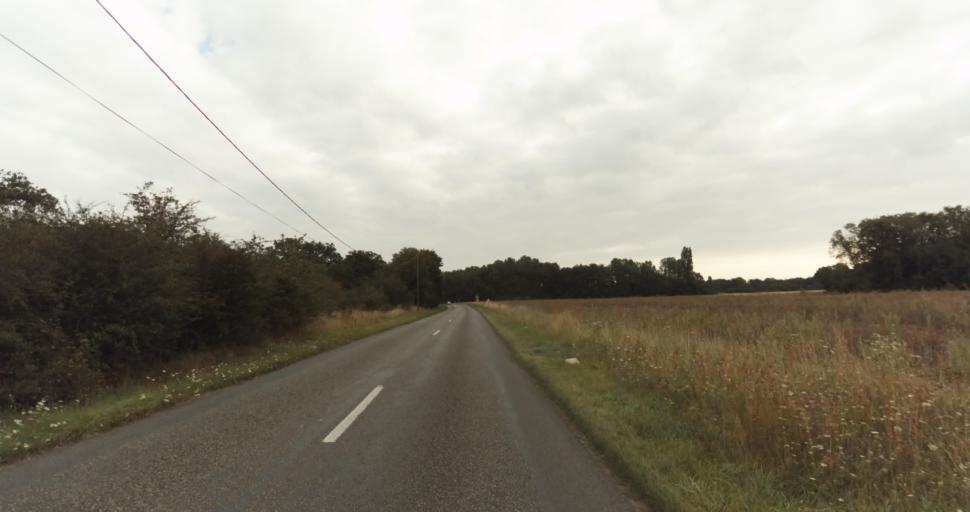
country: FR
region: Haute-Normandie
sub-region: Departement de l'Eure
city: Croth
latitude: 48.8523
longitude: 1.3848
